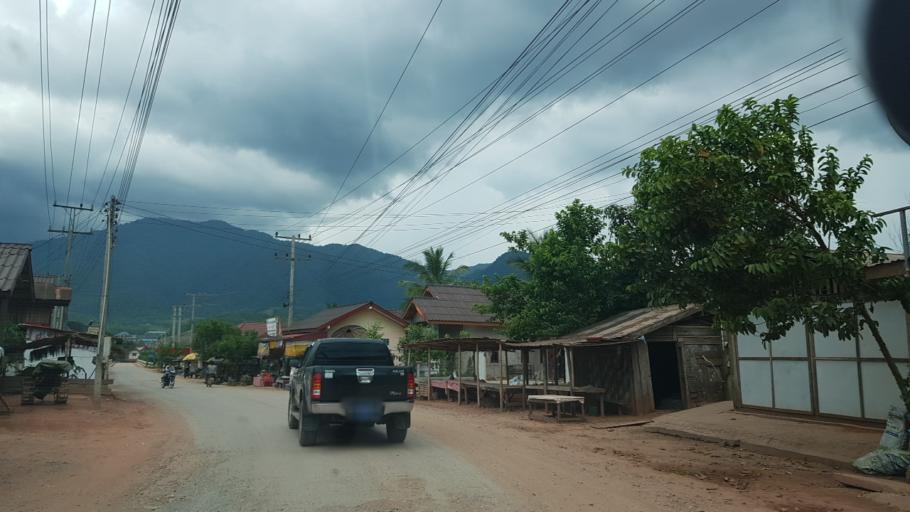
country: LA
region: Oudomxai
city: Muang Xay
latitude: 20.6633
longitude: 101.9729
